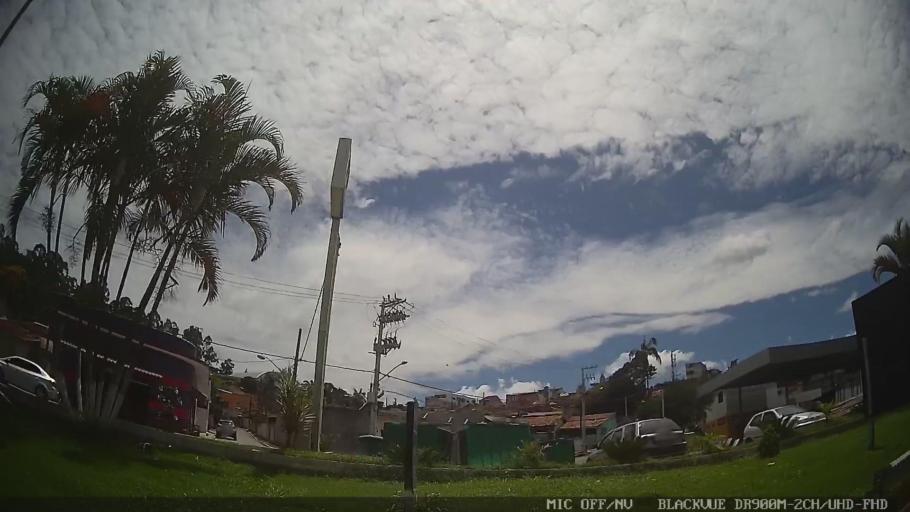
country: BR
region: Sao Paulo
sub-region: Biritiba-Mirim
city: Biritiba Mirim
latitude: -23.5501
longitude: -45.9655
